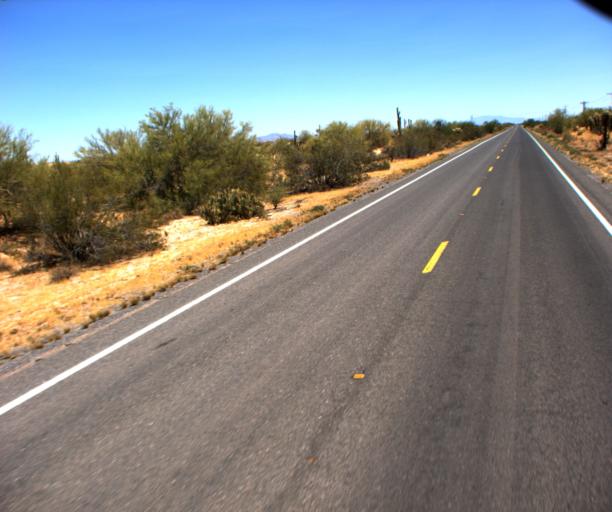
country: US
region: Arizona
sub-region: Pinal County
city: Florence
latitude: 32.9470
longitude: -111.3226
